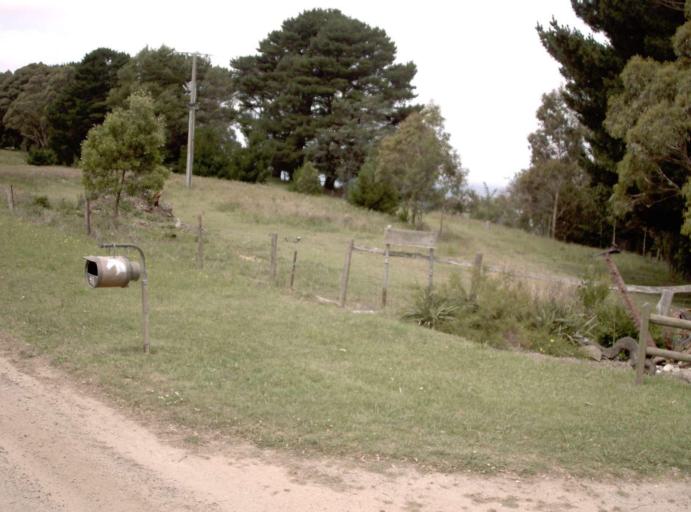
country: AU
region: Victoria
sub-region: Latrobe
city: Traralgon
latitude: -38.3732
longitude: 146.6871
